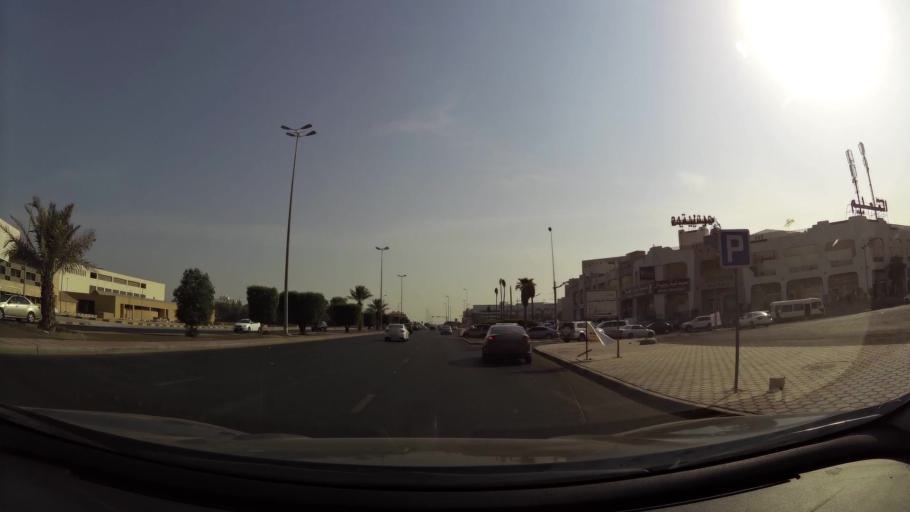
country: KW
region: Al Ahmadi
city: Al Fintas
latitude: 29.1709
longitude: 48.1003
